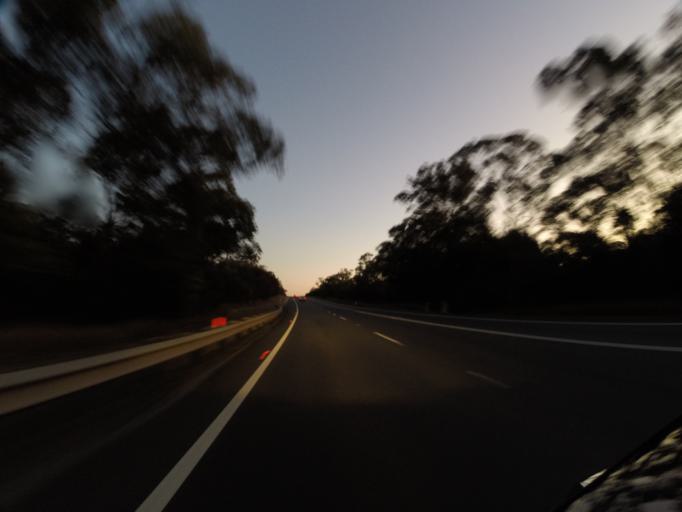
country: AU
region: New South Wales
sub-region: Liverpool
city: Holsworthy
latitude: -34.0301
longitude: 150.9631
